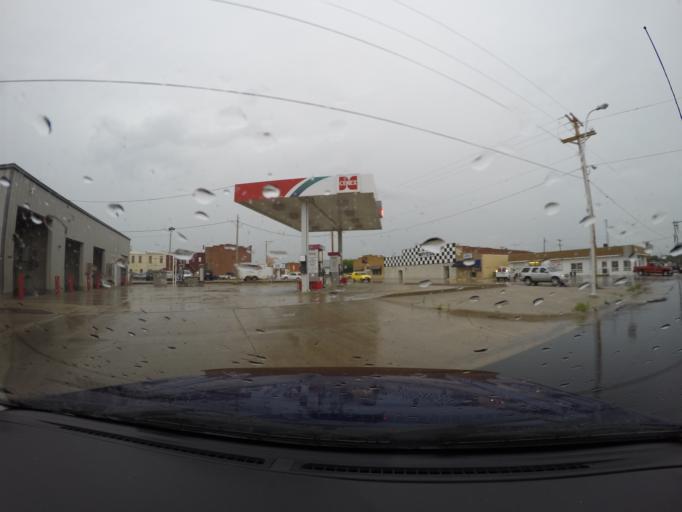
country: US
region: Kansas
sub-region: Cloud County
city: Concordia
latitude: 39.5723
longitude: -97.6594
